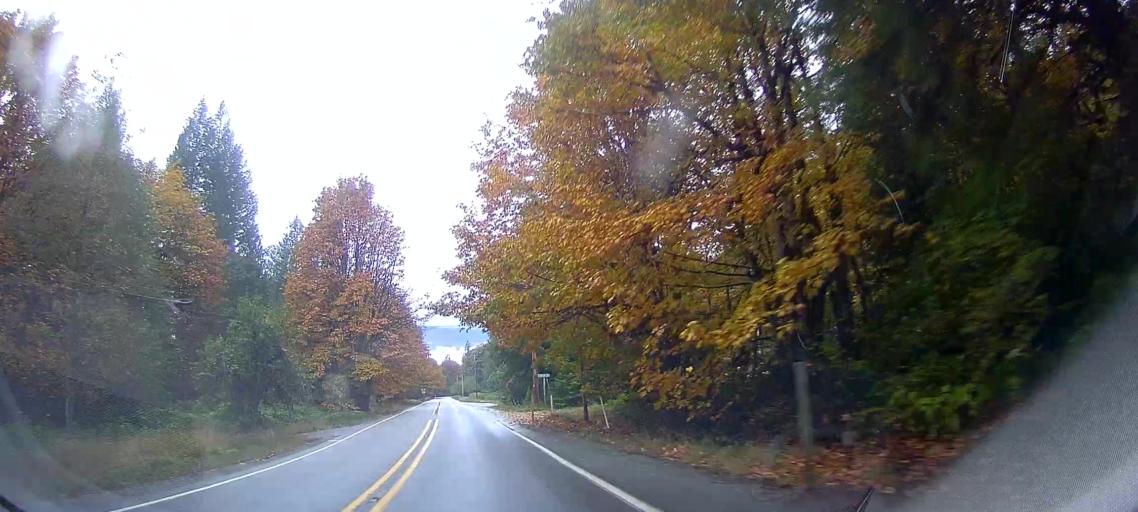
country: US
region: Washington
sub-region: Snohomish County
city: Darrington
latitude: 48.4914
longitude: -121.5743
